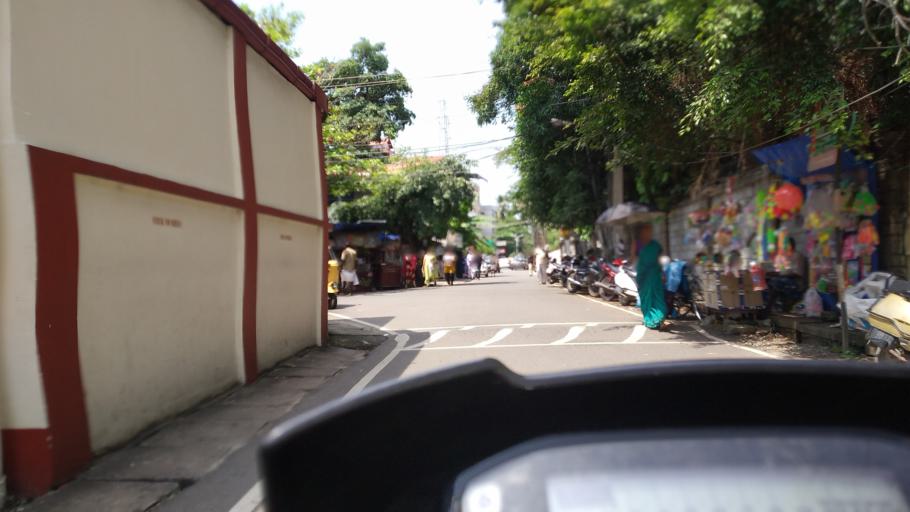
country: IN
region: Kerala
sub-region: Ernakulam
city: Cochin
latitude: 9.9665
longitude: 76.2839
